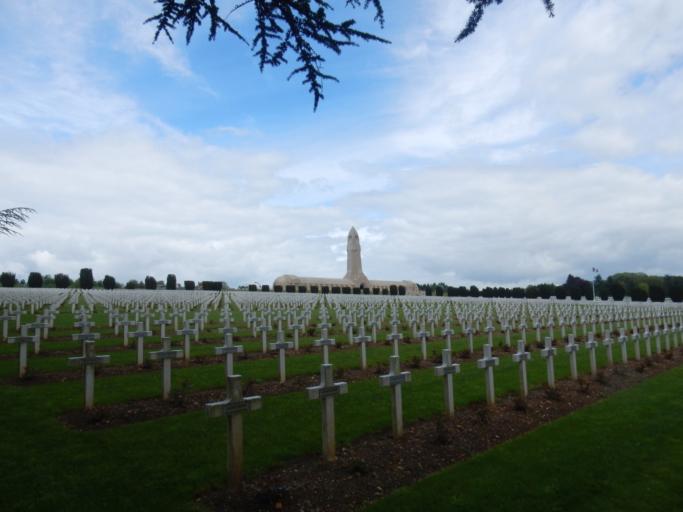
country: FR
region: Lorraine
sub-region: Departement de la Meuse
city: Verdun
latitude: 49.2054
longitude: 5.4229
